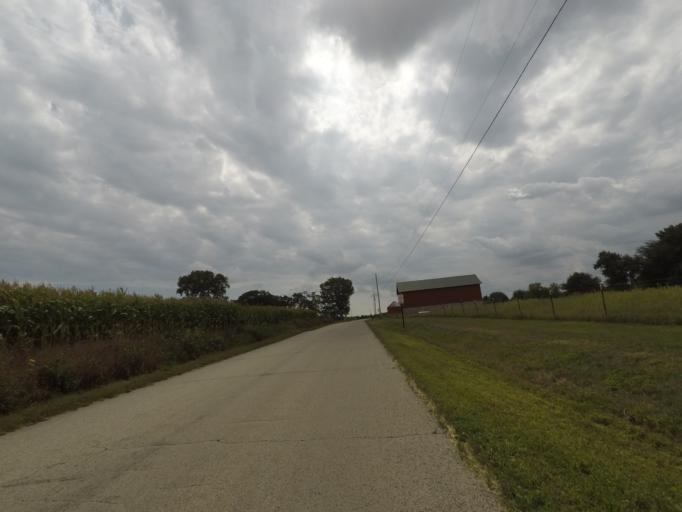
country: US
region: Wisconsin
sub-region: Jefferson County
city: Lake Koshkonong
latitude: 42.8971
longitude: -88.8747
